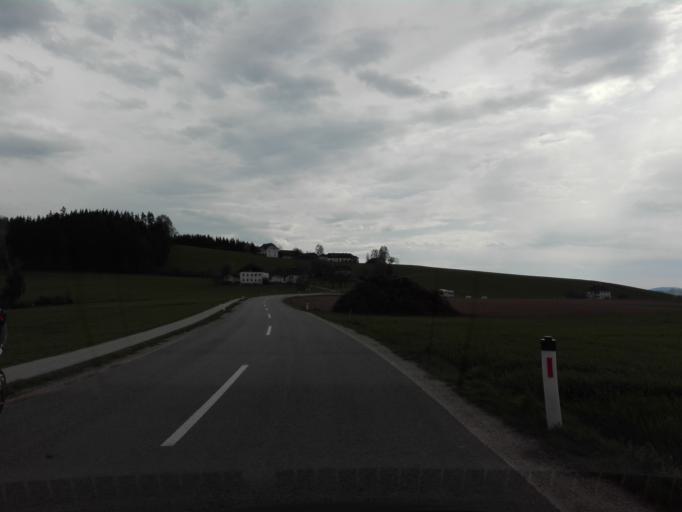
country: AT
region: Upper Austria
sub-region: Politischer Bezirk Rohrbach
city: Schlaegl
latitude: 48.5633
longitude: 13.9750
